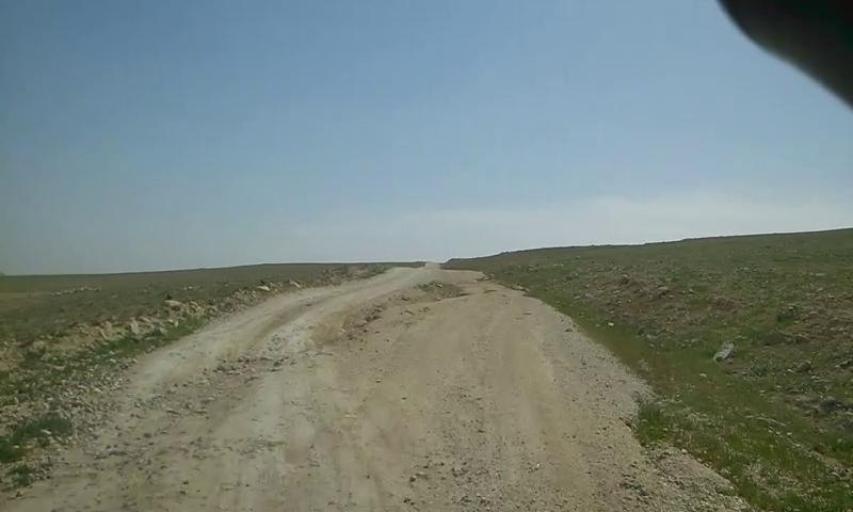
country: PS
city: `Arab ar Rashaydah
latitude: 31.5234
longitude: 35.2961
